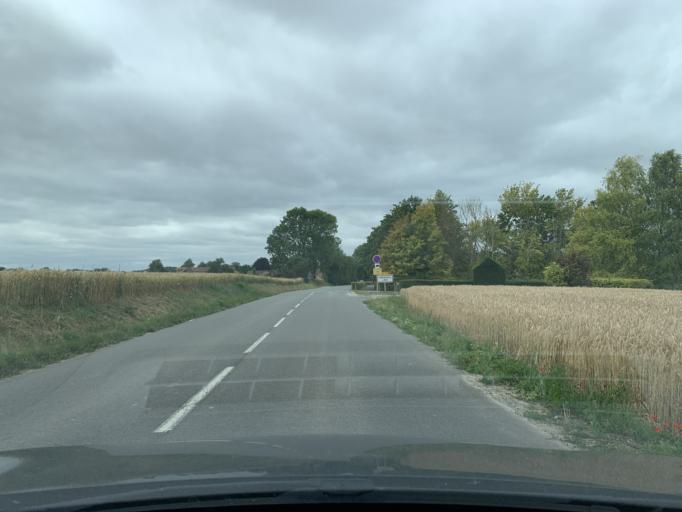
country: FR
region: Nord-Pas-de-Calais
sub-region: Departement du Nord
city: Aubigny-au-Bac
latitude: 50.2543
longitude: 3.1706
